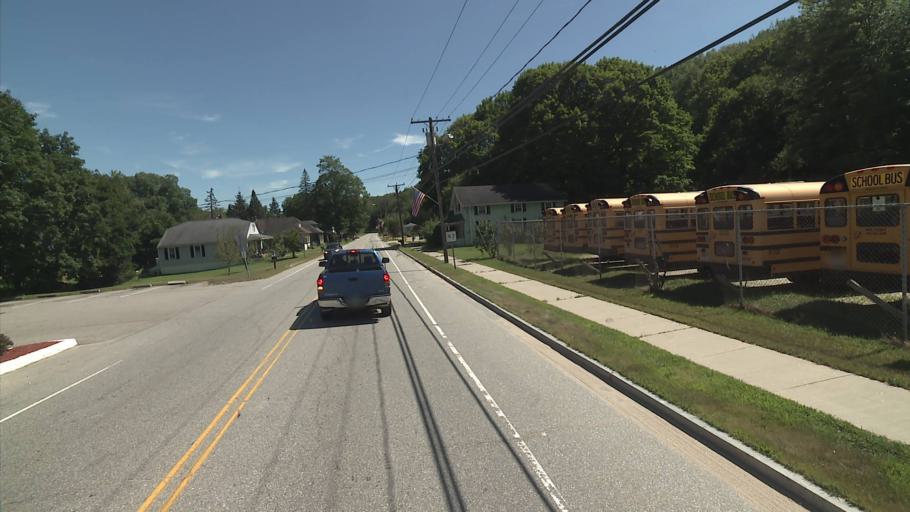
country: US
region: Connecticut
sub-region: New London County
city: Baltic
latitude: 41.6132
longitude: -72.0753
